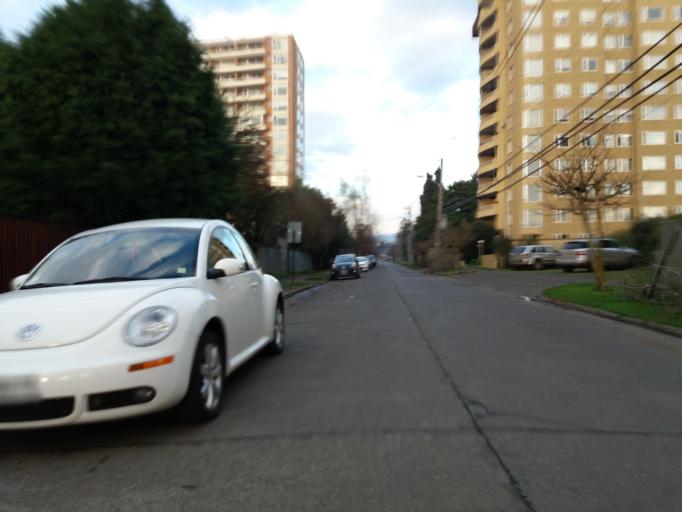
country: CL
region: Araucania
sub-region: Provincia de Cautin
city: Temuco
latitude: -38.7381
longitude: -72.6100
